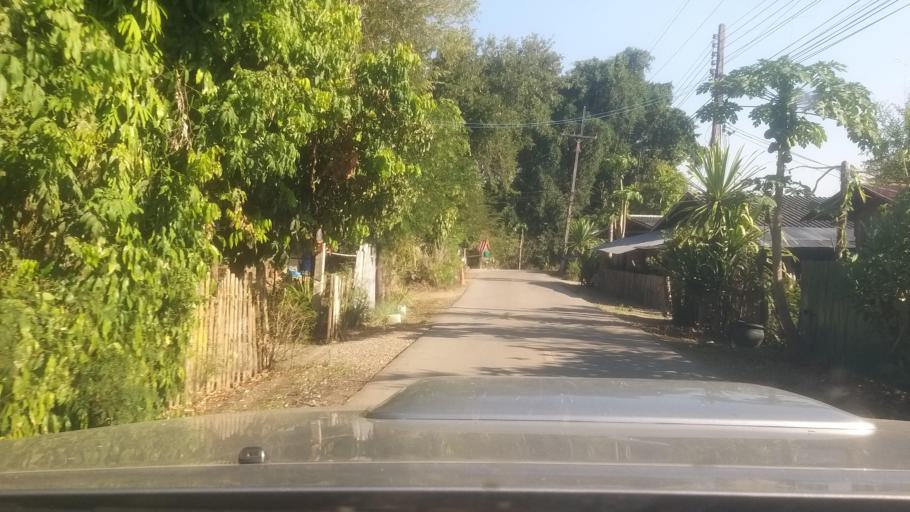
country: TH
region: Phrae
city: Phrae
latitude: 18.2634
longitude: 99.9923
